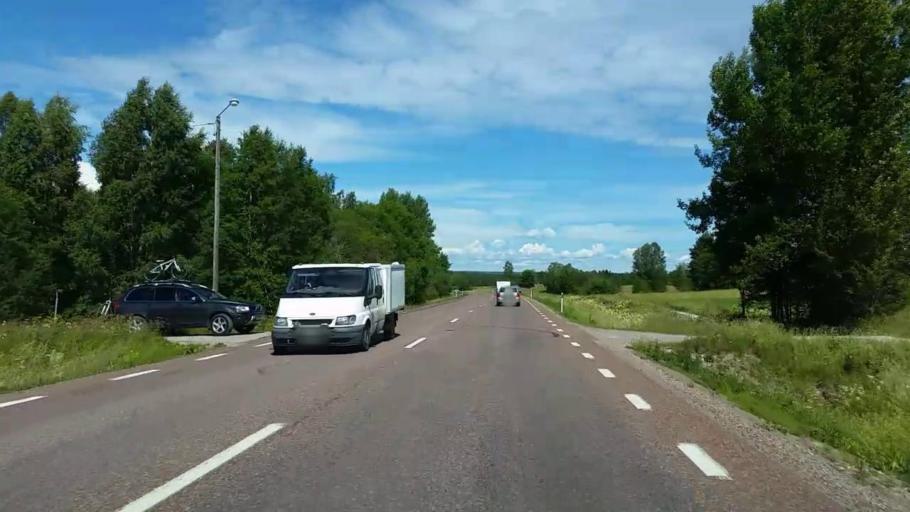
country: SE
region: Dalarna
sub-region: Rattviks Kommun
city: Raettvik
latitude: 60.9370
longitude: 15.2317
